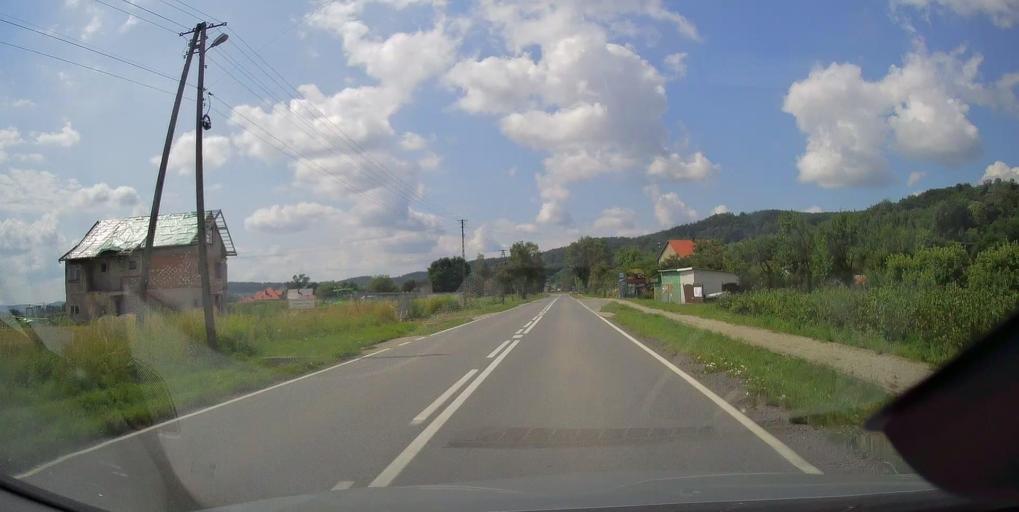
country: PL
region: Lesser Poland Voivodeship
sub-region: Powiat tarnowski
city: Wielka Wies
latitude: 49.9059
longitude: 20.8176
